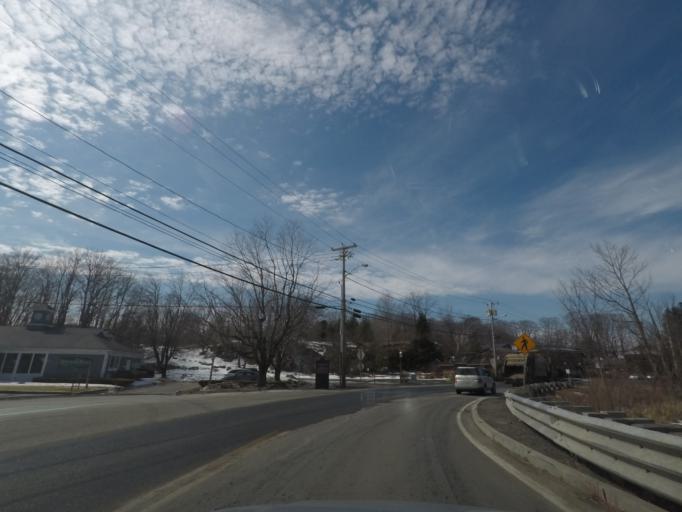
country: US
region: Massachusetts
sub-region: Berkshire County
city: West Stockbridge
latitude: 42.3349
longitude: -73.3682
